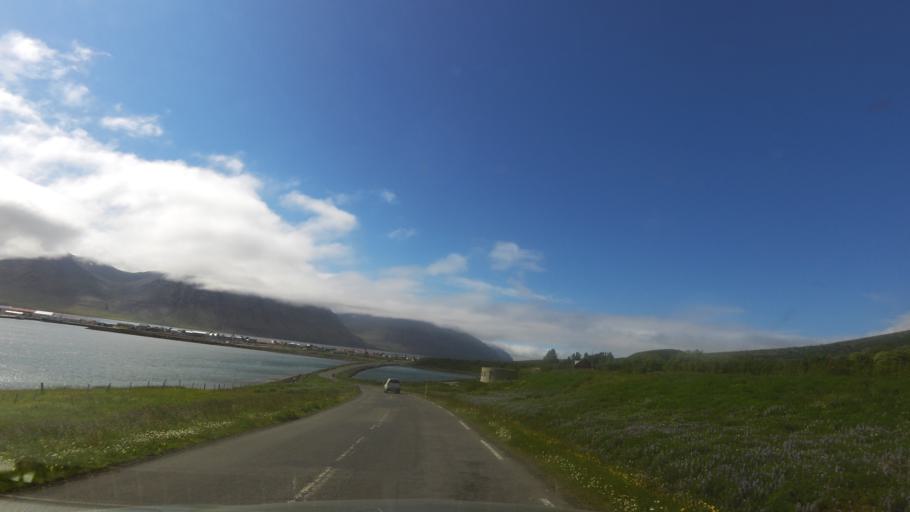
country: IS
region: Westfjords
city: Isafjoerdur
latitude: 66.0518
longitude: -23.4957
